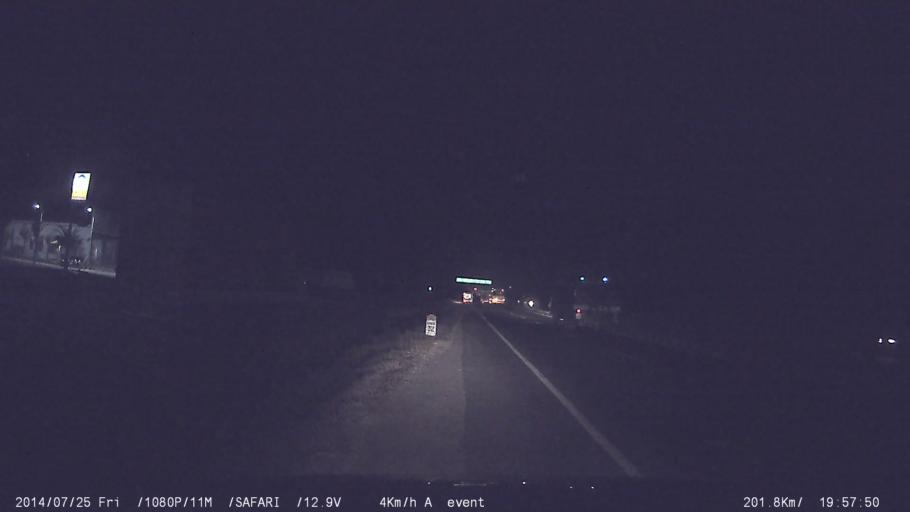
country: IN
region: Tamil Nadu
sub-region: Salem
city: Salem
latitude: 11.6193
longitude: 78.1069
